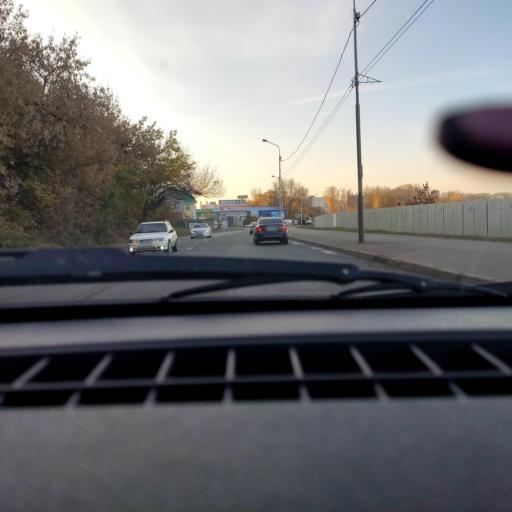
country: RU
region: Bashkortostan
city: Ufa
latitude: 54.7017
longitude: 55.9687
